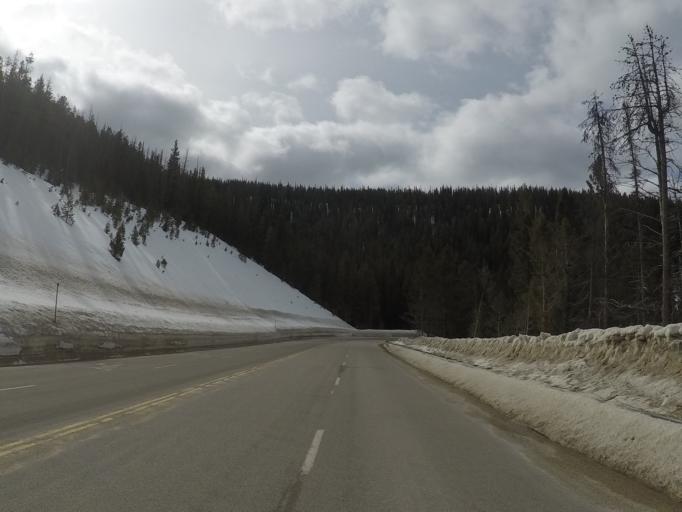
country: US
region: Idaho
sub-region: Lemhi County
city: Salmon
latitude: 45.7065
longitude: -113.9341
